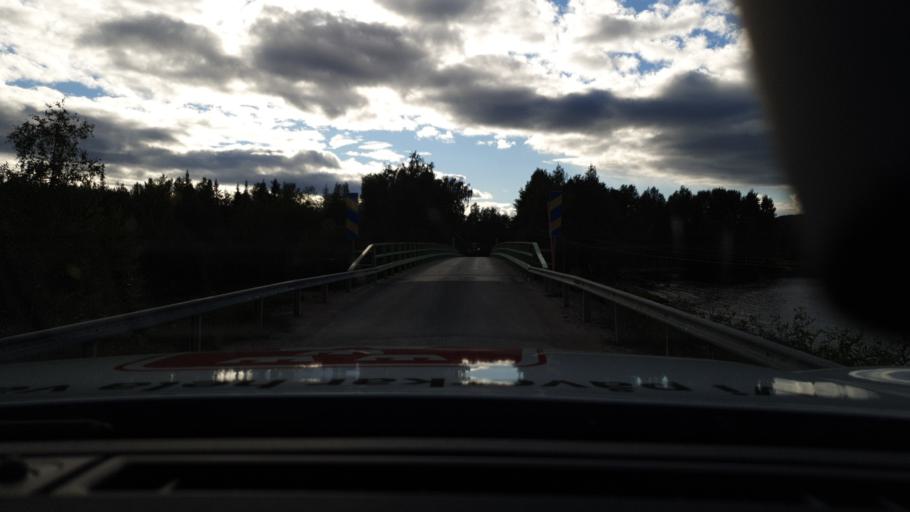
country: SE
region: Norrbotten
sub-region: Overkalix Kommun
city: OEverkalix
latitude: 66.6392
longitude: 22.2324
